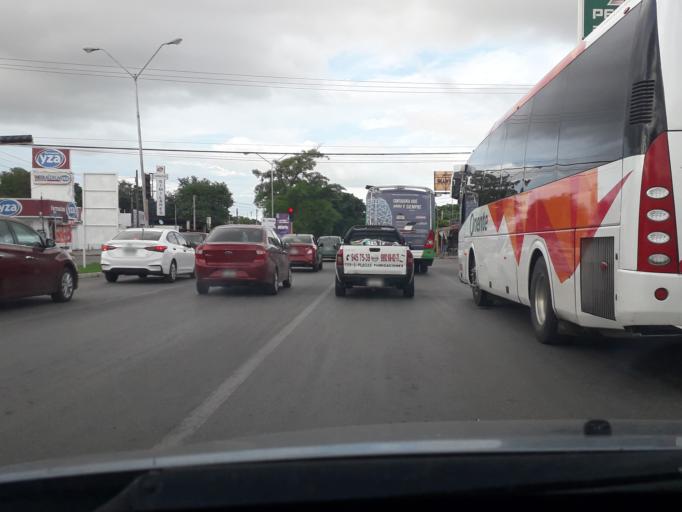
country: MX
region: Yucatan
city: Merida
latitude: 20.9608
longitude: -89.6633
